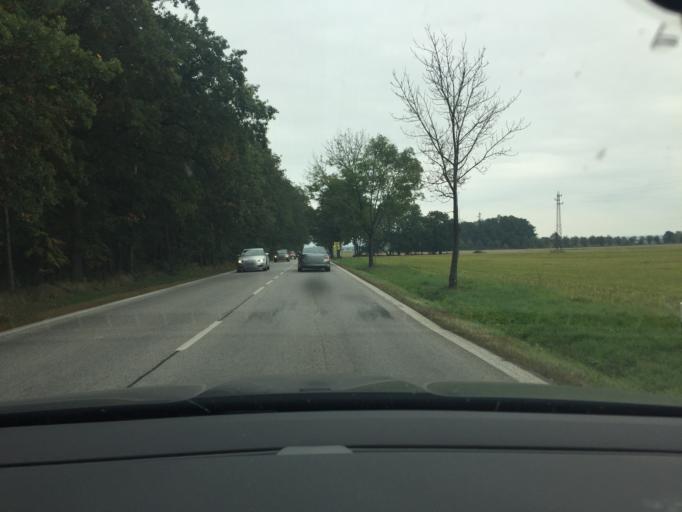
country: CZ
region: Jihocesky
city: Zliv
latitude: 49.0260
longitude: 14.3836
